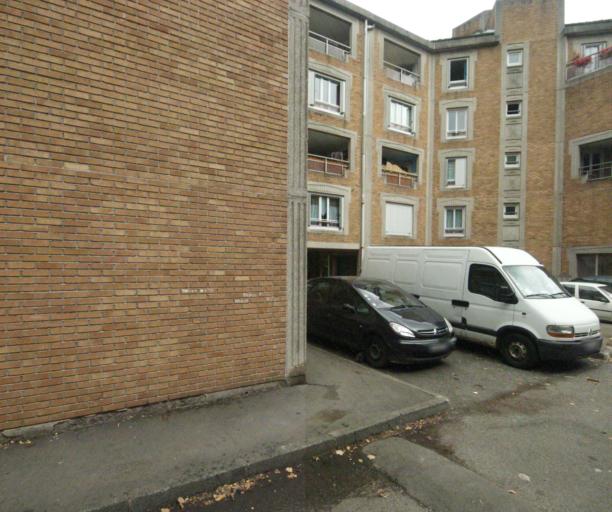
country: FR
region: Nord-Pas-de-Calais
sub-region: Departement du Nord
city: Ronchin
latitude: 50.6187
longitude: 3.0921
